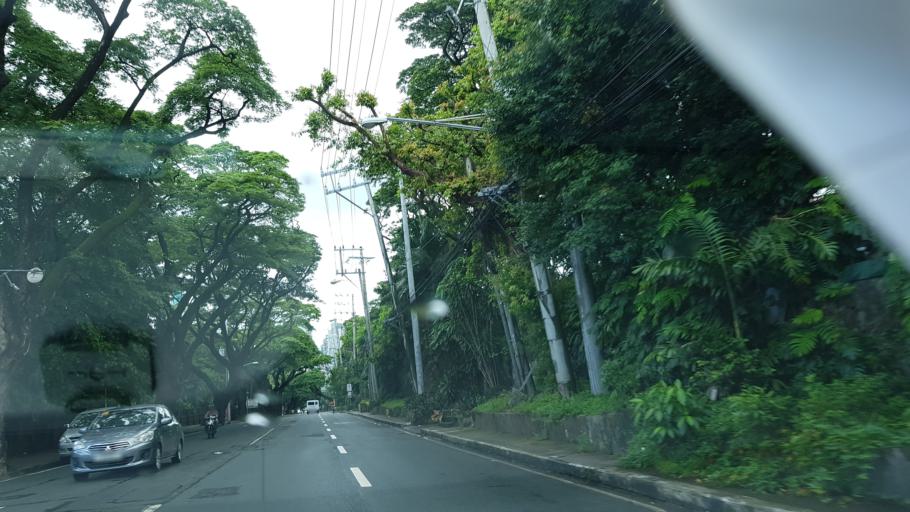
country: PH
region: Metro Manila
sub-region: Makati City
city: Makati City
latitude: 14.5476
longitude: 121.0345
